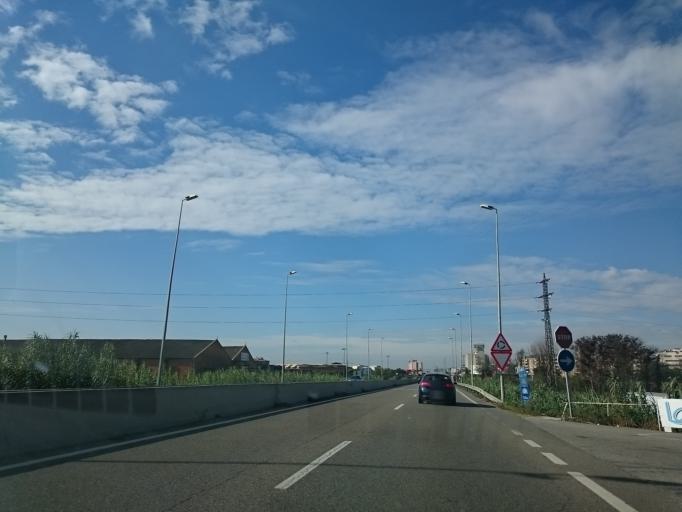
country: ES
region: Catalonia
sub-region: Provincia de Lleida
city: Lleida
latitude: 41.6112
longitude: 0.6426
